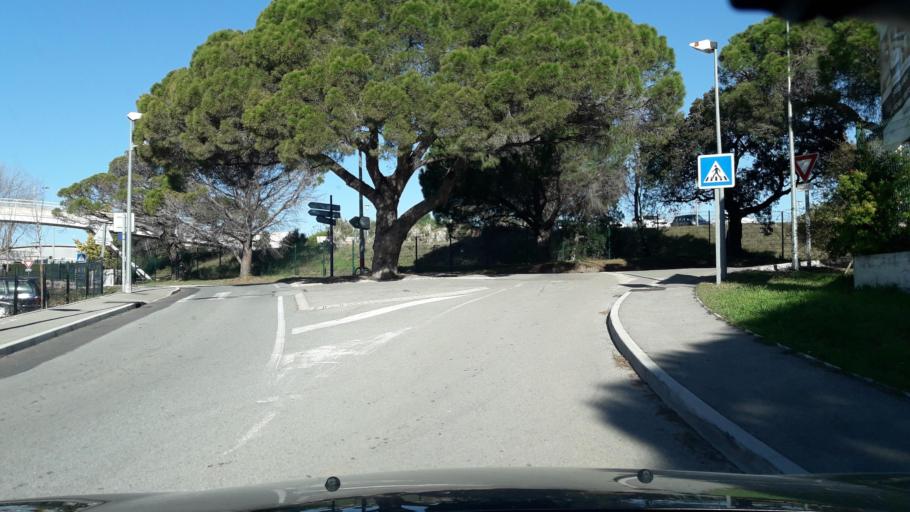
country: FR
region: Provence-Alpes-Cote d'Azur
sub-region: Departement du Var
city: Frejus
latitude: 43.4439
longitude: 6.7572
